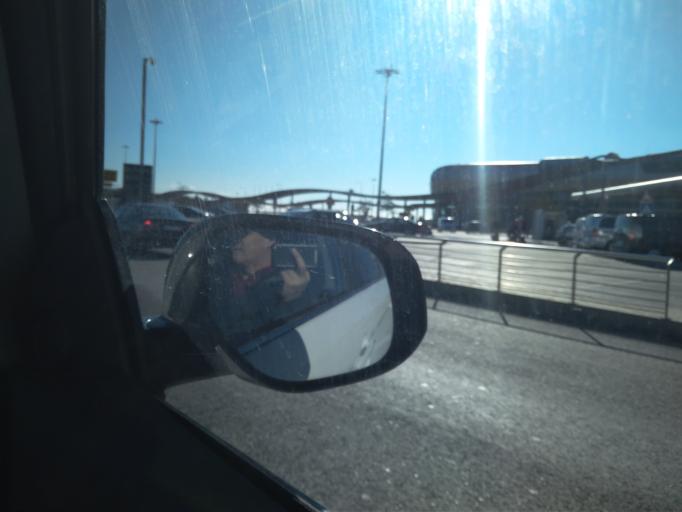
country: PT
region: Faro
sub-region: Faro
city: Faro
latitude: 37.0215
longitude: -7.9673
